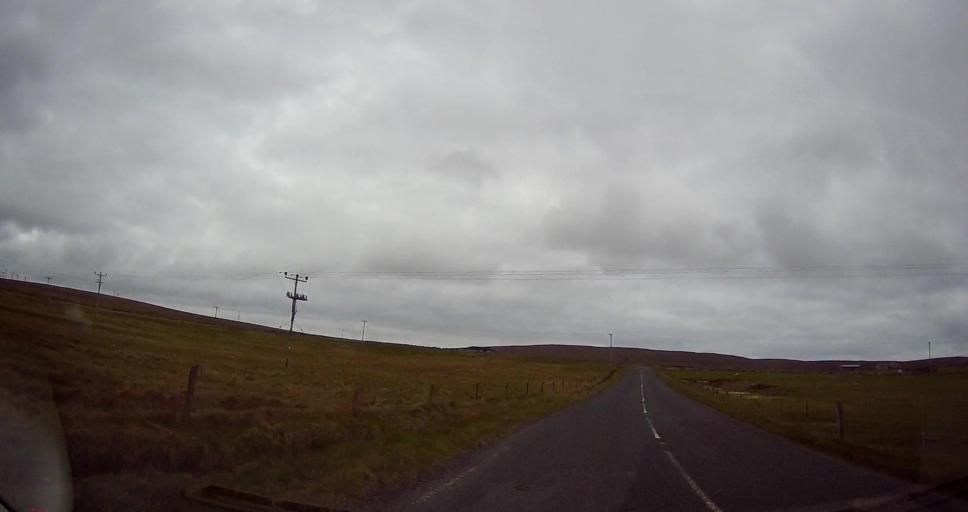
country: GB
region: Scotland
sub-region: Shetland Islands
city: Shetland
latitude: 60.7555
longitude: -0.8779
